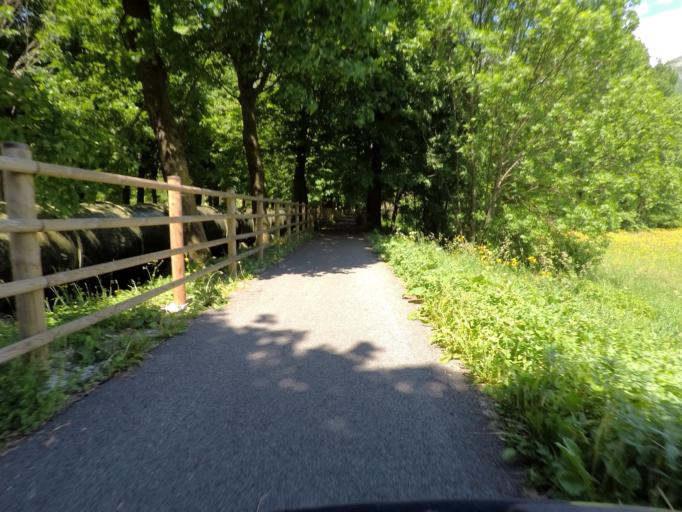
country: IT
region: Friuli Venezia Giulia
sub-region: Provincia di Udine
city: Lauco
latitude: 46.4071
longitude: 12.9471
